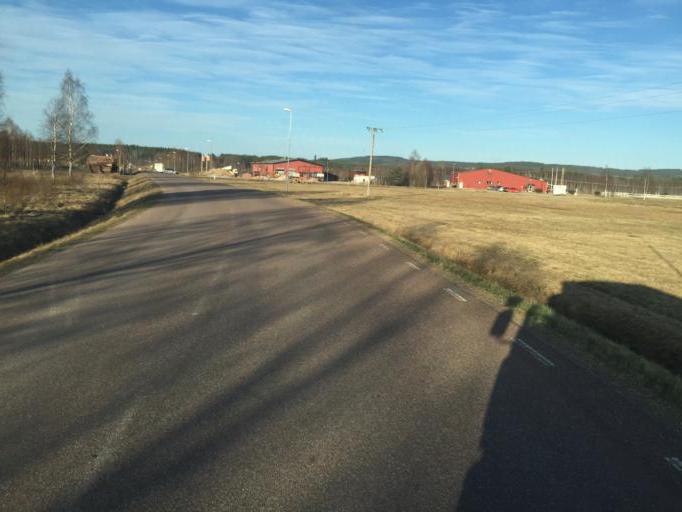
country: SE
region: Dalarna
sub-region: Gagnefs Kommun
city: Mockfjard
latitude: 60.4938
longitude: 14.9645
